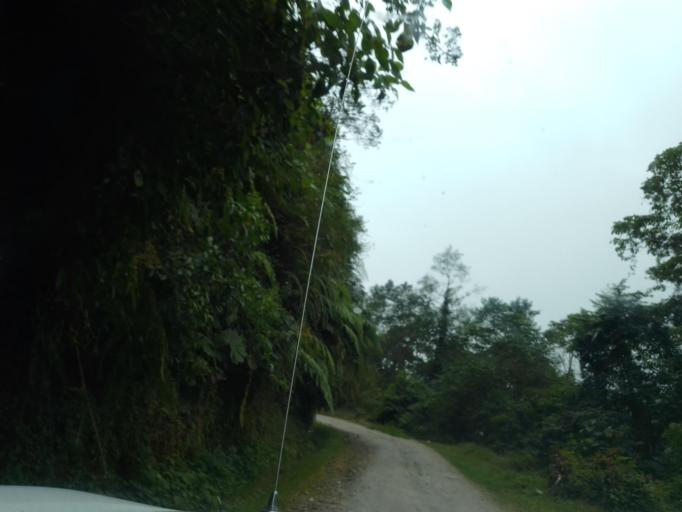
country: MX
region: Chiapas
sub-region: Union Juarez
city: Santo Domingo
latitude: 15.0925
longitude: -92.0922
